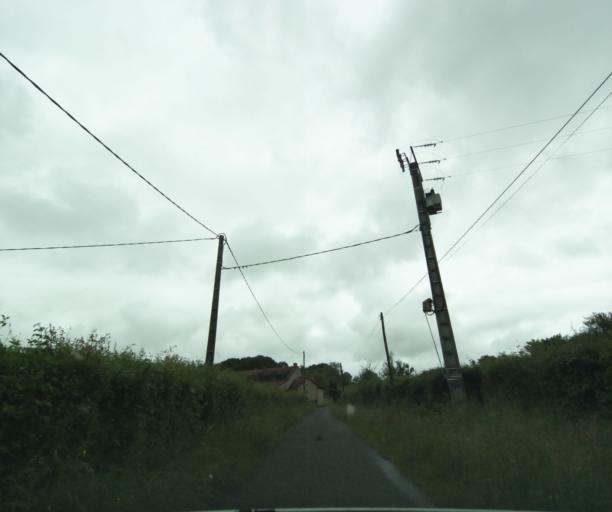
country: FR
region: Bourgogne
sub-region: Departement de Saone-et-Loire
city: Charolles
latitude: 46.4664
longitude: 4.3328
